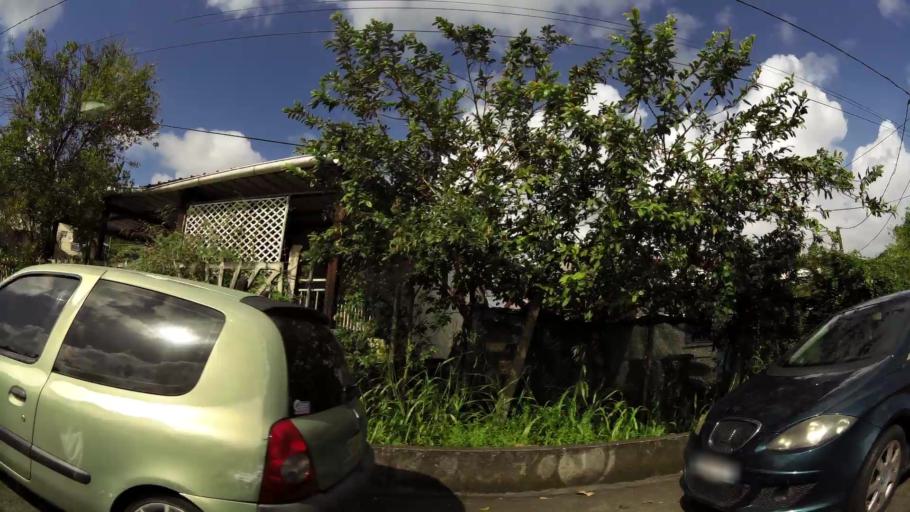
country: MQ
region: Martinique
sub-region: Martinique
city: Le Lamentin
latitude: 14.6193
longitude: -60.9978
